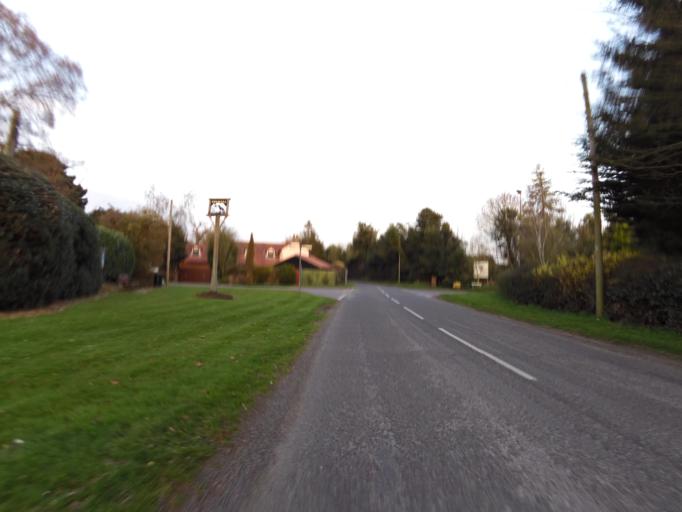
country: GB
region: England
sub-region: Suffolk
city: Kesgrave
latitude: 52.0345
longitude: 1.2377
